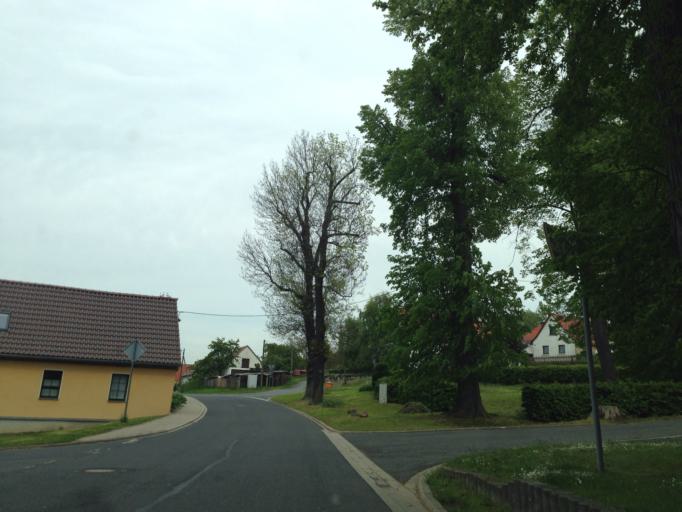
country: DE
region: Thuringia
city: Seisla
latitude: 50.6516
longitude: 11.5432
